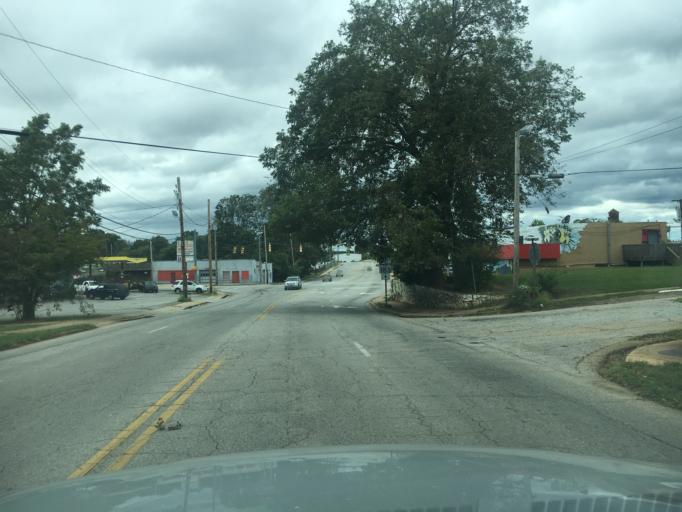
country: US
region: South Carolina
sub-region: Greenville County
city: Sans Souci
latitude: 34.8670
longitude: -82.4095
